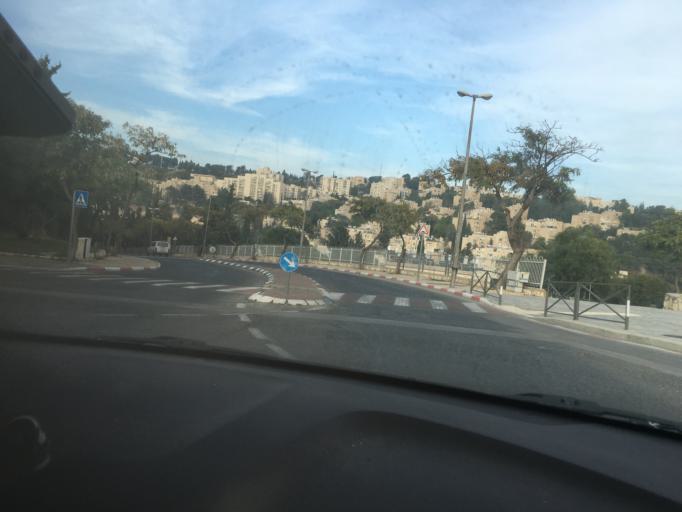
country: PS
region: West Bank
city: Ash Shaykh Sa`d
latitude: 31.7462
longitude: 35.2328
